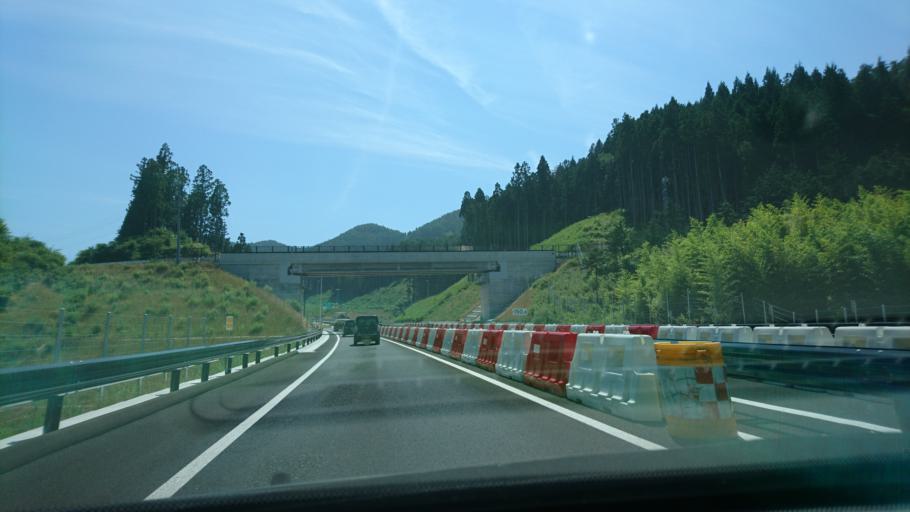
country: JP
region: Iwate
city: Ofunato
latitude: 38.9886
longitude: 141.6123
